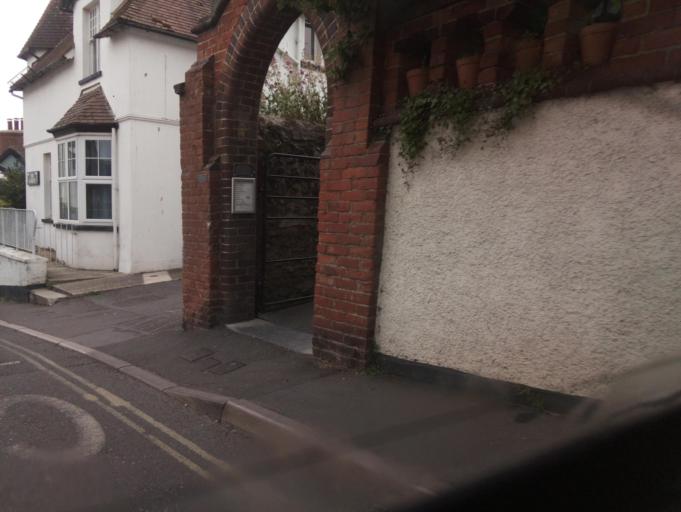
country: GB
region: England
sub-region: Dorset
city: Lyme Regis
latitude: 50.7259
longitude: -2.9321
